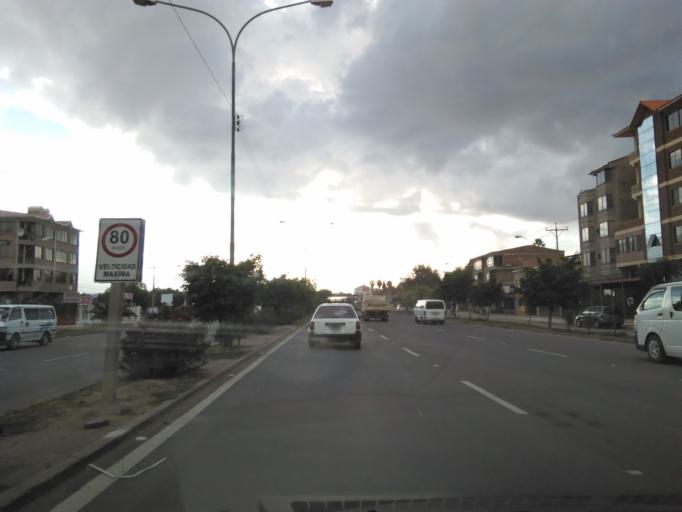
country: BO
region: Cochabamba
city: Cochabamba
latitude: -17.3923
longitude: -66.2071
